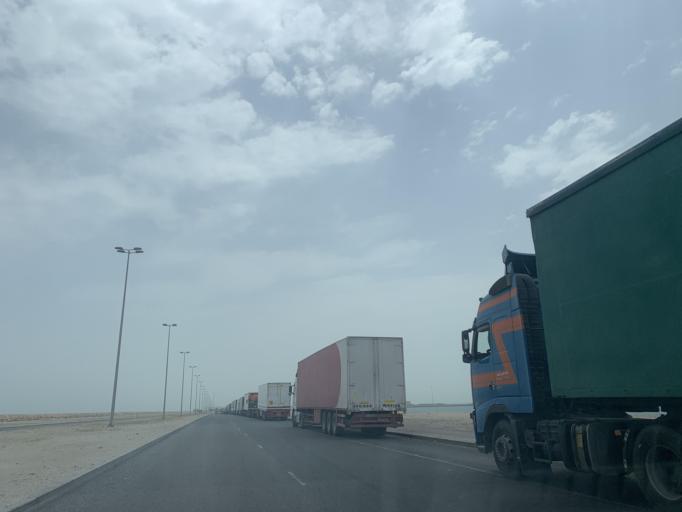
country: BH
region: Muharraq
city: Al Hadd
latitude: 26.2062
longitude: 50.7066
